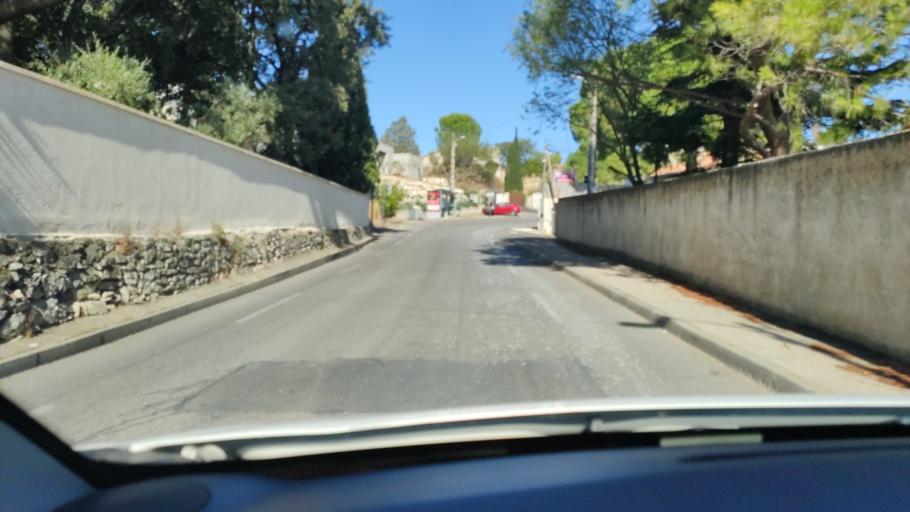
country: FR
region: Languedoc-Roussillon
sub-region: Departement du Gard
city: Villeneuve-les-Avignon
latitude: 43.9758
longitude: 4.7890
